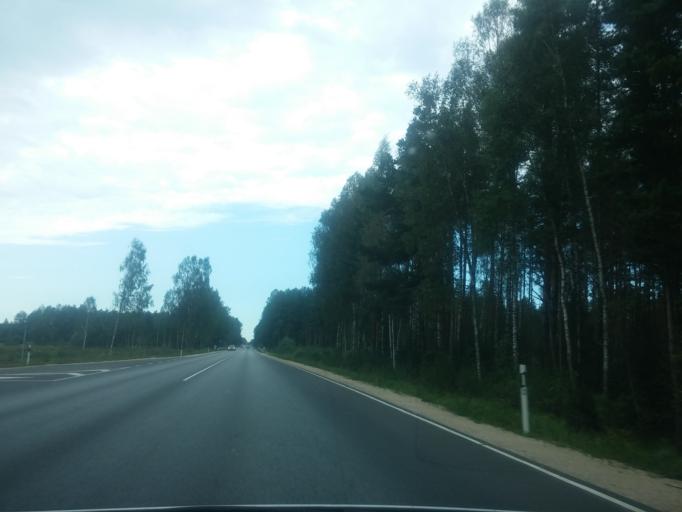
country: LV
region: Ikskile
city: Ikskile
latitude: 56.8778
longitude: 24.5212
